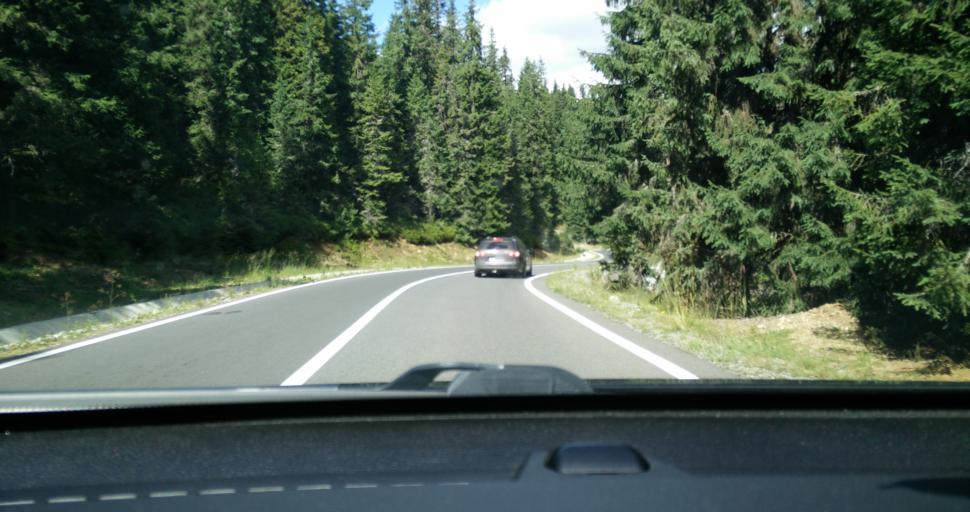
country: RO
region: Hunedoara
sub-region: Oras Petrila
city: Petrila
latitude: 45.4795
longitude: 23.6354
